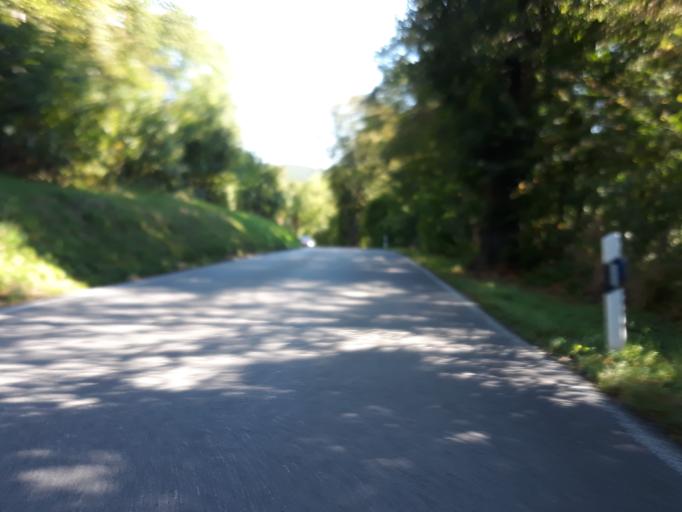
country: DE
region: Baden-Wuerttemberg
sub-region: Karlsruhe Region
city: Gechingen
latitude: 48.7064
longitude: 8.8383
